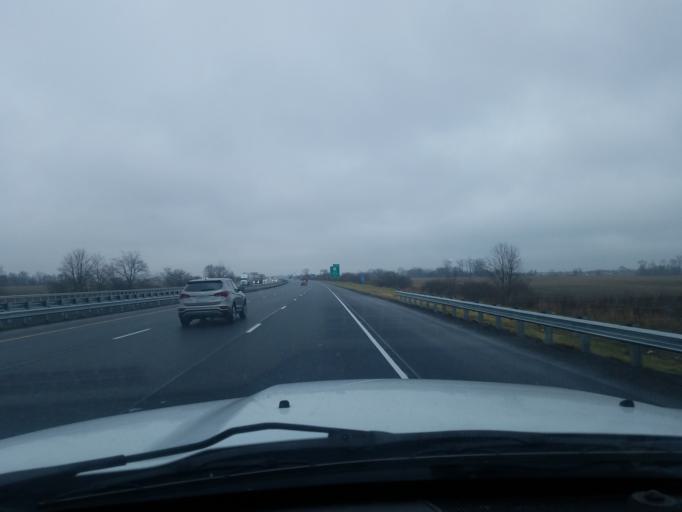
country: US
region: Indiana
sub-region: Hancock County
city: Fortville
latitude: 39.9918
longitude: -85.8717
